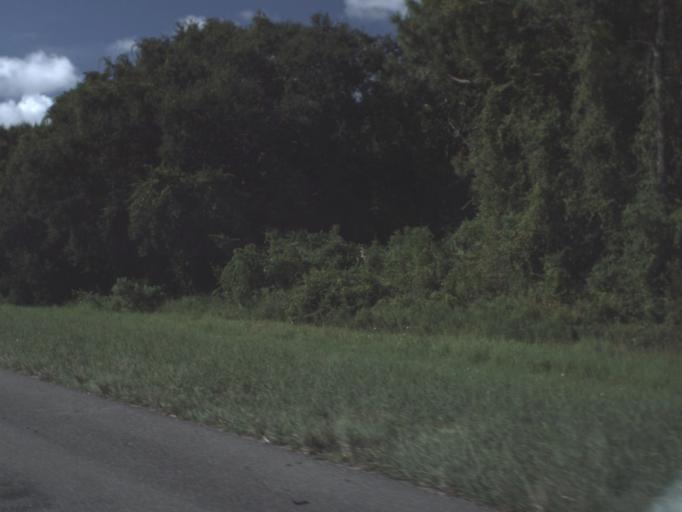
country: US
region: Florida
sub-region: Sarasota County
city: Desoto Lakes
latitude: 27.4194
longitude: -82.4576
